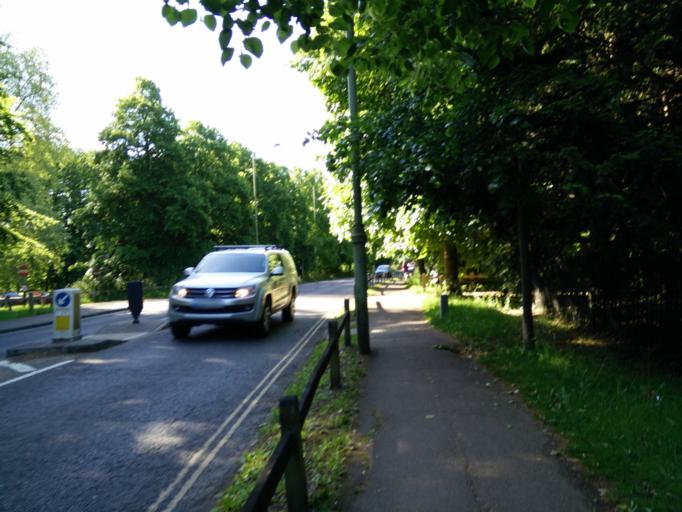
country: GB
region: England
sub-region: Cambridgeshire
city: Cambridge
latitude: 52.2071
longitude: 0.1109
